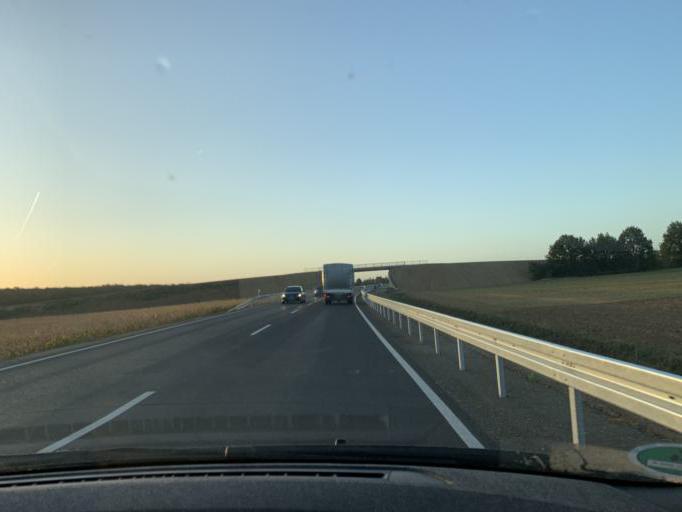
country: DE
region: North Rhine-Westphalia
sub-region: Regierungsbezirk Koln
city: Vettweiss
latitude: 50.7302
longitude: 6.5700
